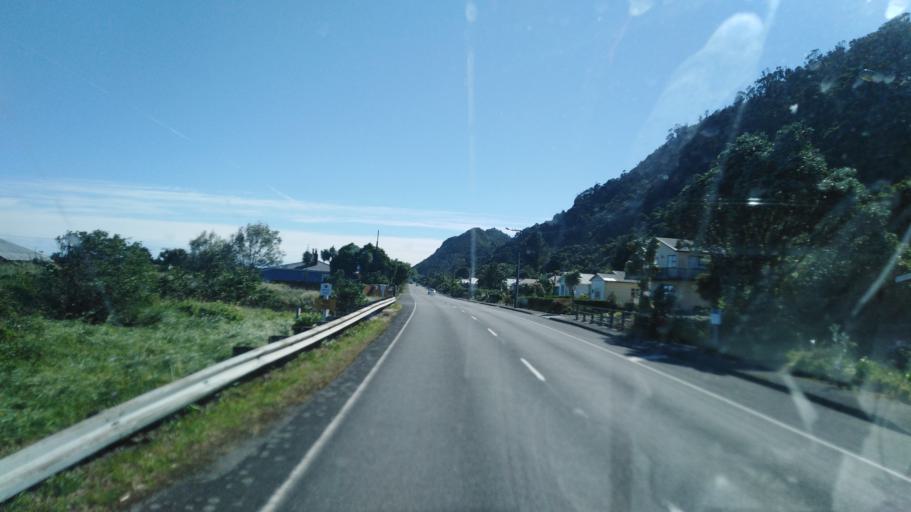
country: NZ
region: West Coast
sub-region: Buller District
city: Westport
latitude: -41.6375
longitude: 171.8473
